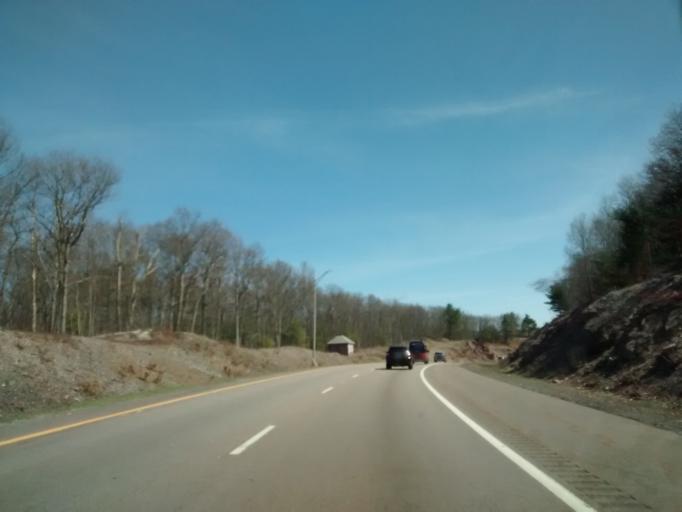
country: US
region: Massachusetts
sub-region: Norfolk County
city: Milton
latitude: 42.2018
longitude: -71.0825
